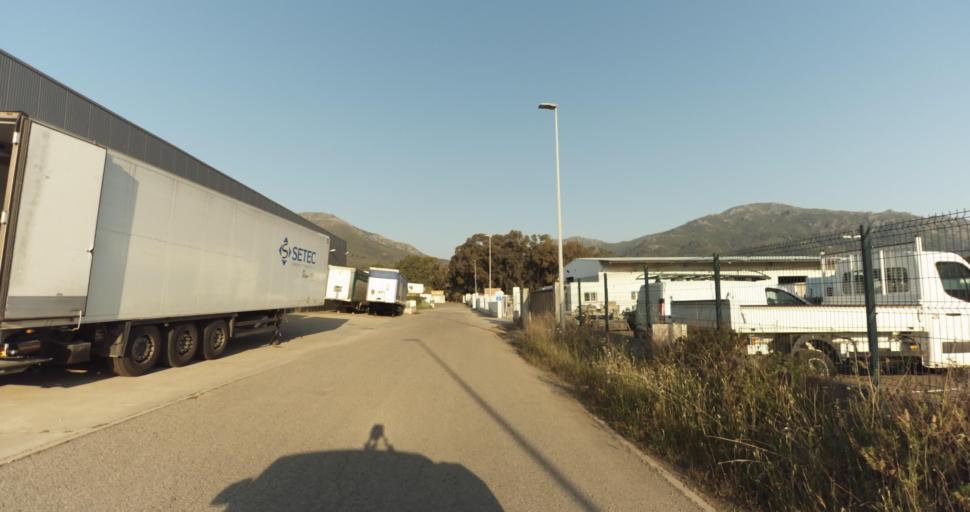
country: FR
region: Corsica
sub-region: Departement de la Haute-Corse
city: Biguglia
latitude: 42.6008
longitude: 9.4410
